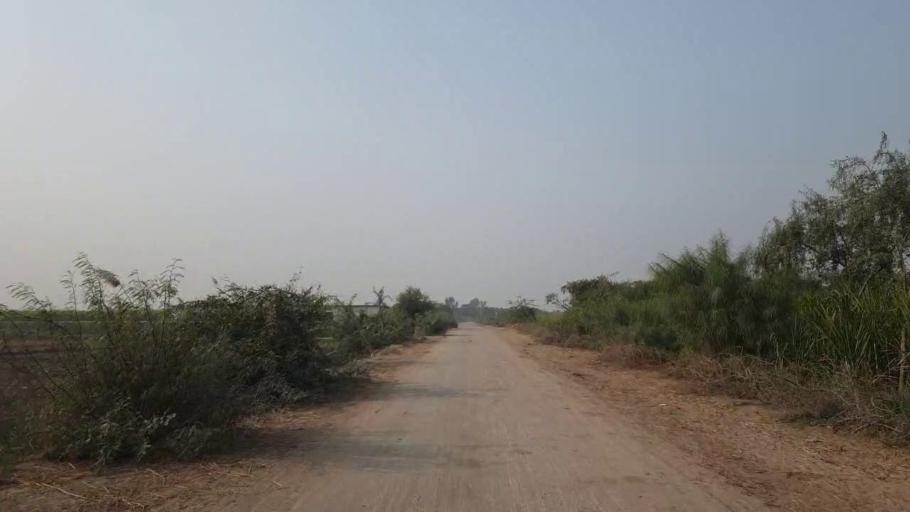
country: PK
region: Sindh
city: Tando Muhammad Khan
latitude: 25.1387
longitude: 68.6146
